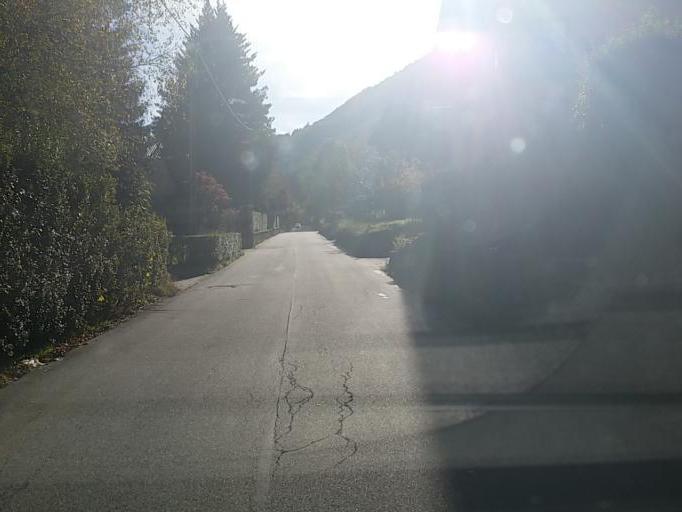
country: IT
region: Piedmont
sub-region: Provincia Verbano-Cusio-Ossola
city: Malesco
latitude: 46.1244
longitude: 8.5034
